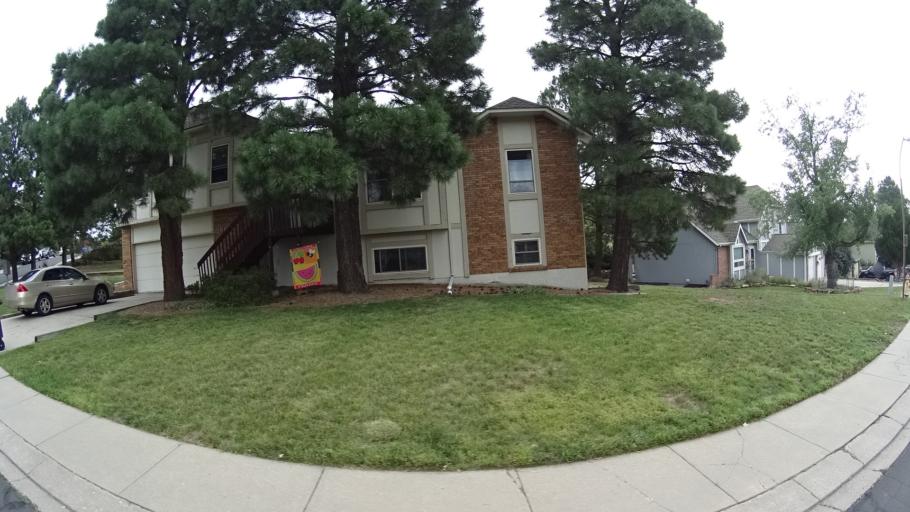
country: US
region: Colorado
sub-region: El Paso County
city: Air Force Academy
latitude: 38.9276
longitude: -104.8443
